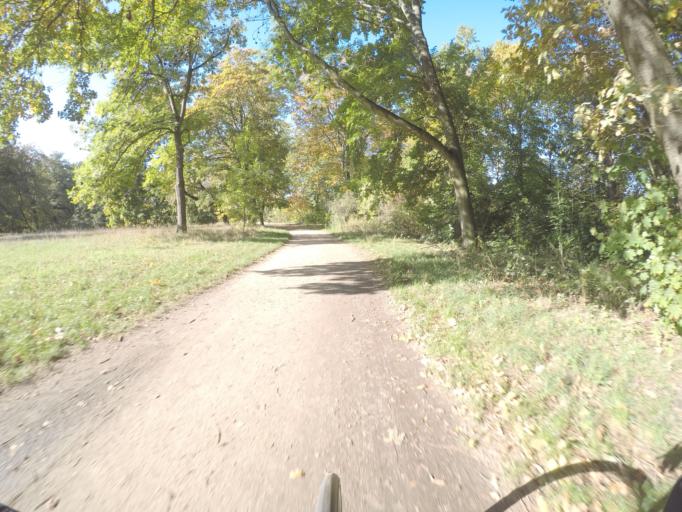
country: DE
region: Berlin
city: Charlottenburg-Nord
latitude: 52.5271
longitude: 13.2874
